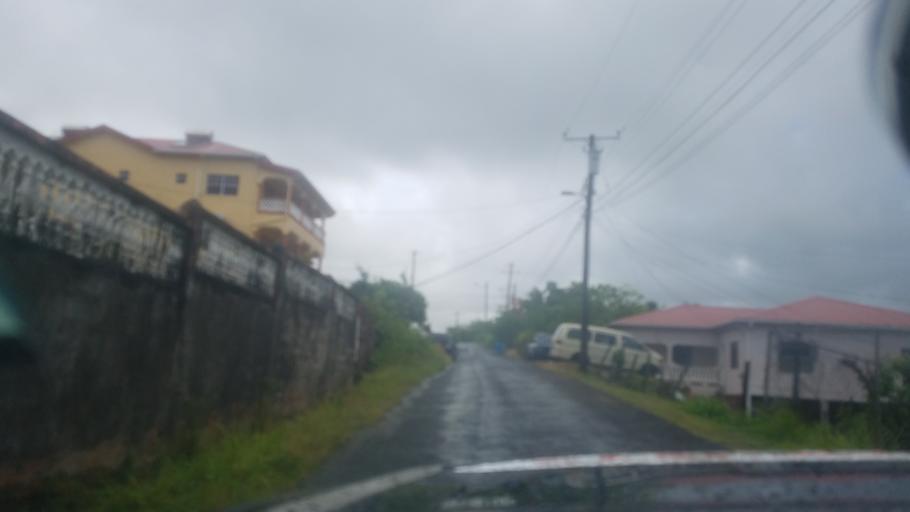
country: LC
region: Laborie Quarter
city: Laborie
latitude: 13.7468
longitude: -60.9672
